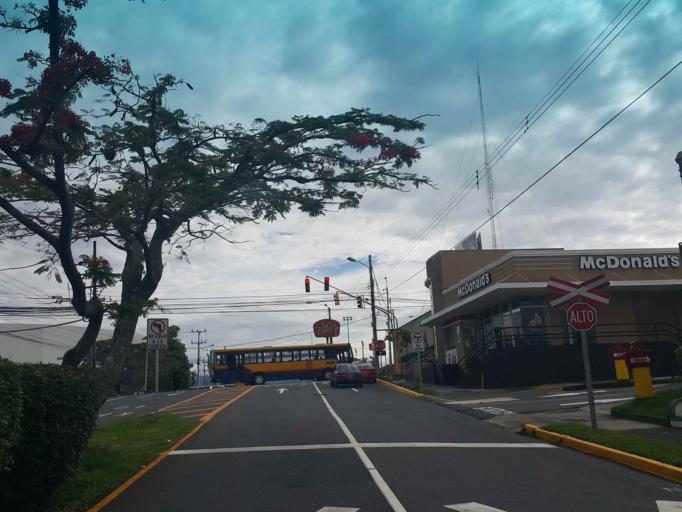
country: CR
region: San Jose
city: San Jose
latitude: 9.9316
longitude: -84.0984
